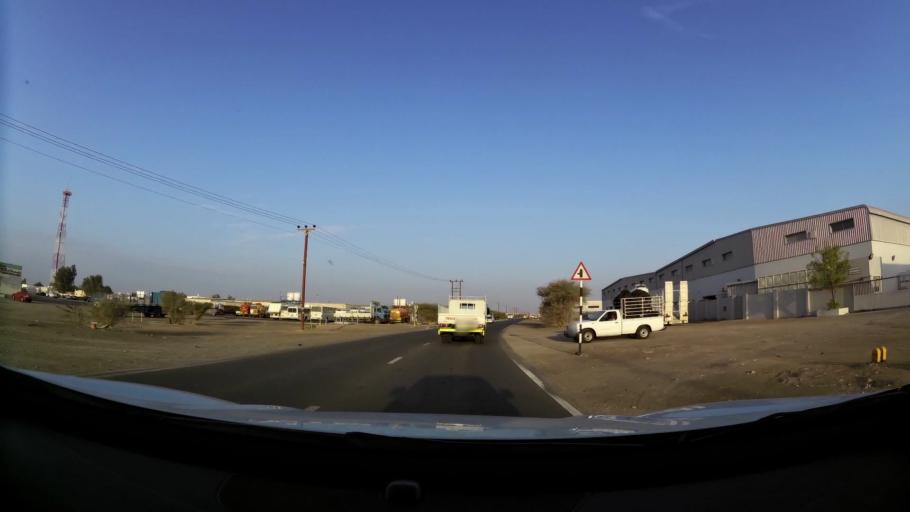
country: AE
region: Abu Dhabi
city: Al Ain
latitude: 24.1493
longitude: 55.8125
